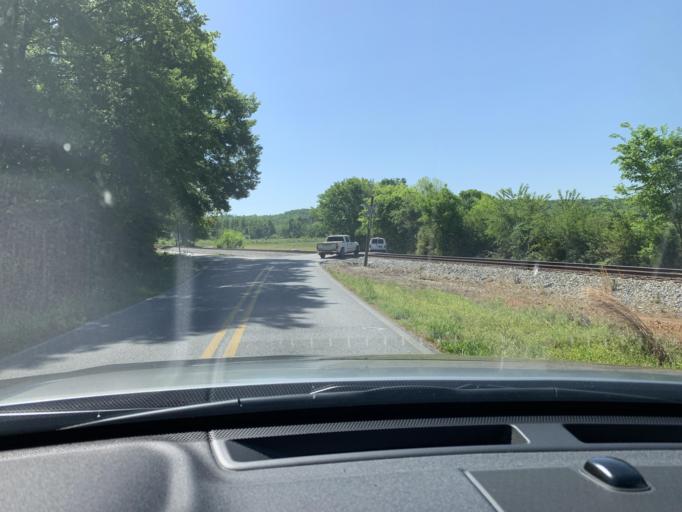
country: US
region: Georgia
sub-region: Polk County
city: Cedartown
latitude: 33.9374
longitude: -85.2101
